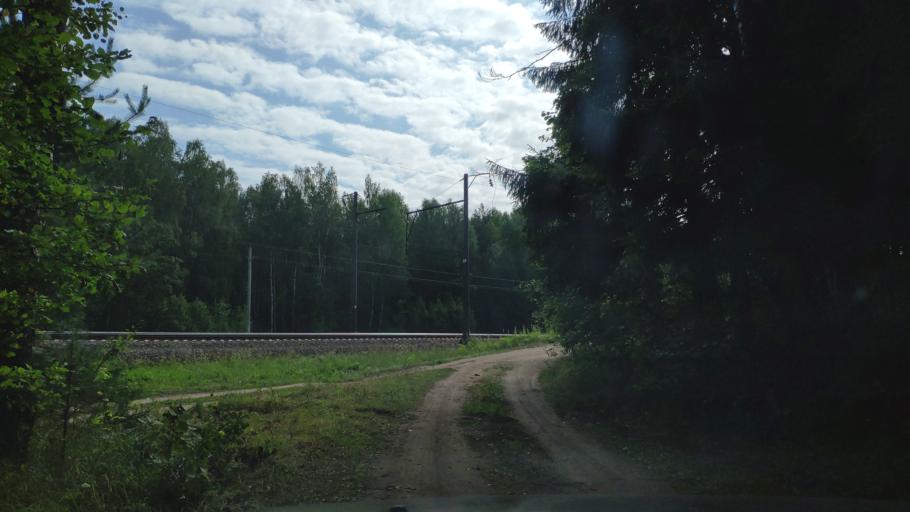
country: BY
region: Minsk
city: Khatsyezhyna
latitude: 53.9601
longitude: 27.3071
